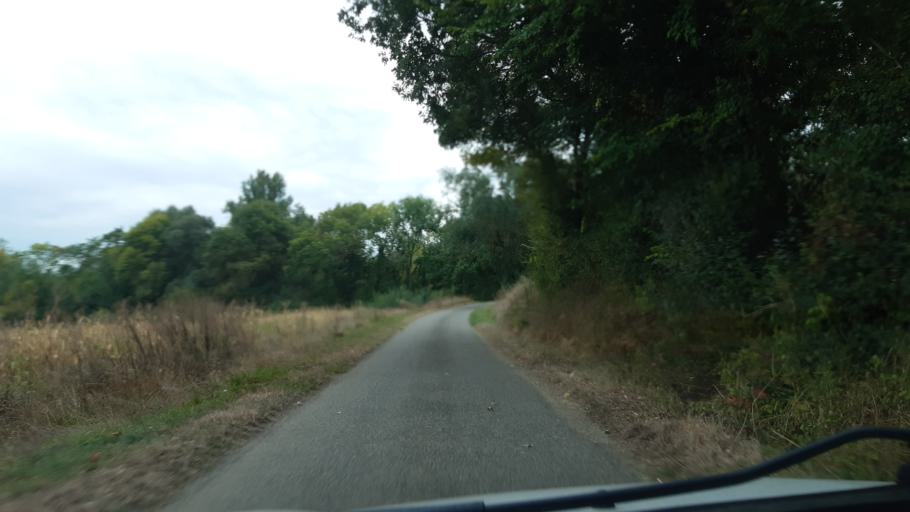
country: FR
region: Midi-Pyrenees
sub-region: Departement du Gers
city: Gimont
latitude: 43.6906
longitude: 0.9725
